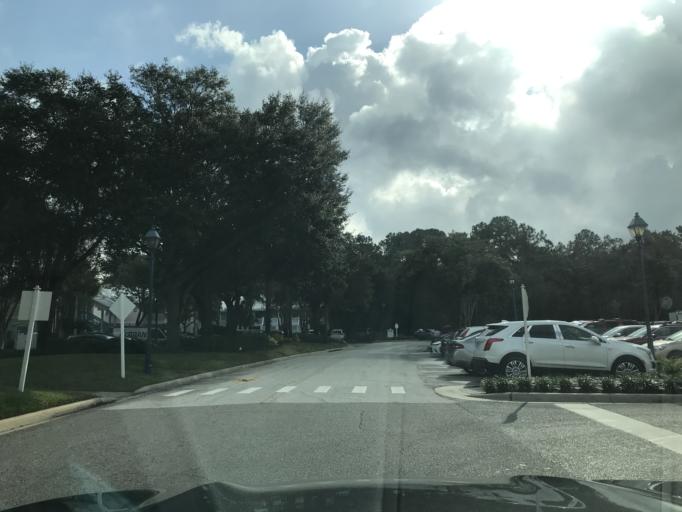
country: US
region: Florida
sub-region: Osceola County
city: Celebration
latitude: 28.3756
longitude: -81.5330
